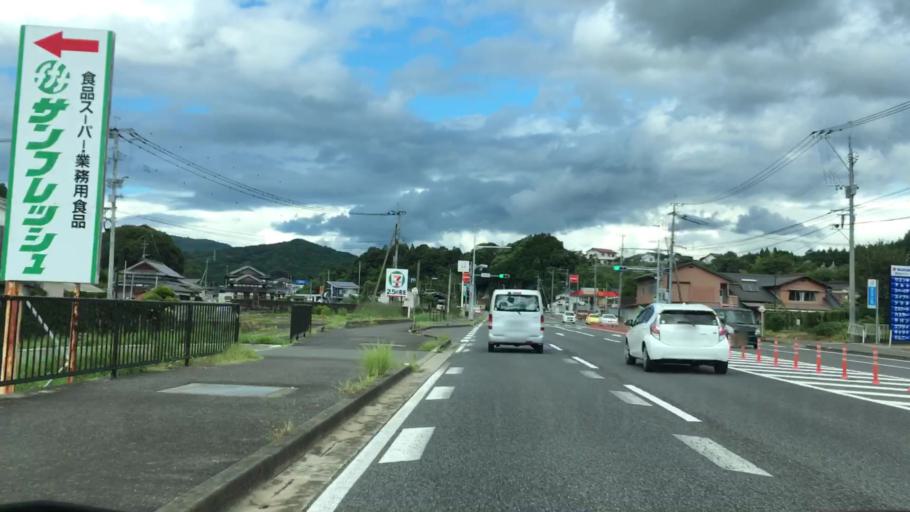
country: JP
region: Saga Prefecture
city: Imaricho-ko
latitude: 33.2748
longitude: 129.8926
